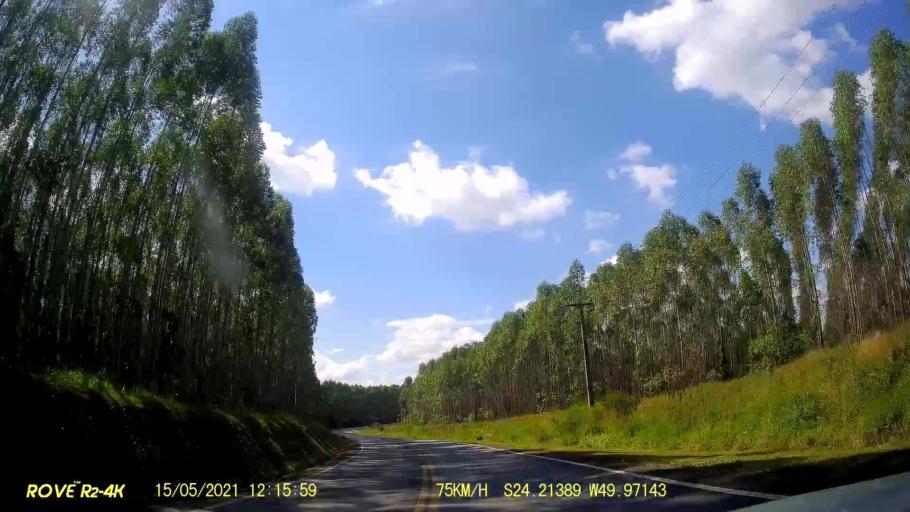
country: BR
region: Parana
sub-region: Jaguariaiva
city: Jaguariaiva
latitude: -24.2140
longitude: -49.9717
